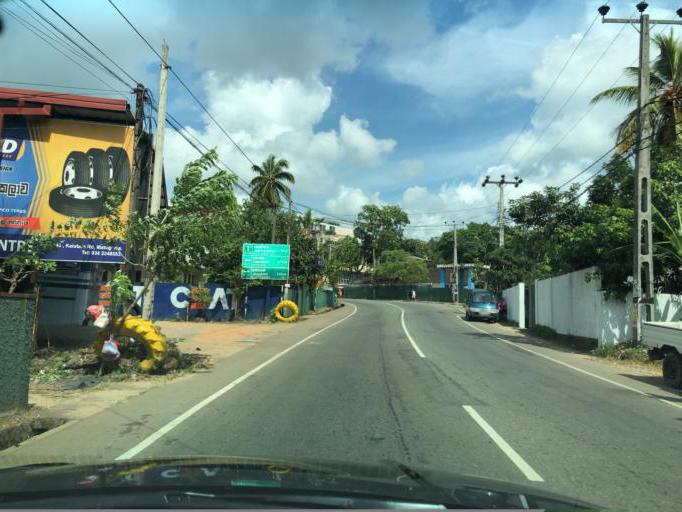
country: LK
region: Western
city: Horawala Junction
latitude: 6.5224
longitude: 80.1106
